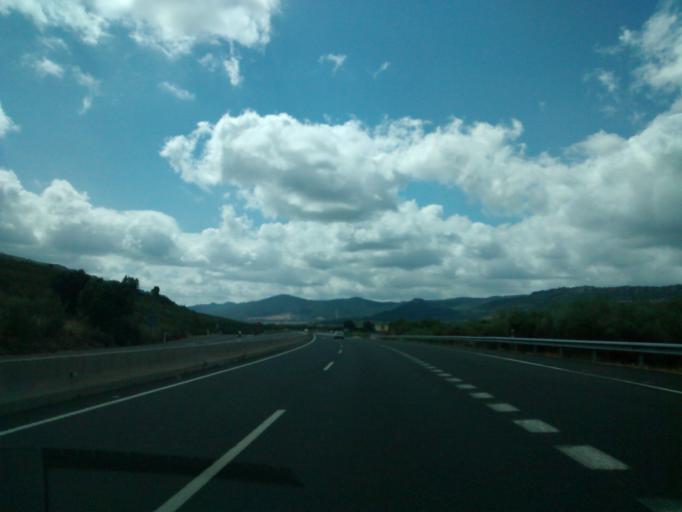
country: ES
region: Extremadura
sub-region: Provincia de Caceres
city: Casas de Miravete
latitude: 39.7344
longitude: -5.7224
